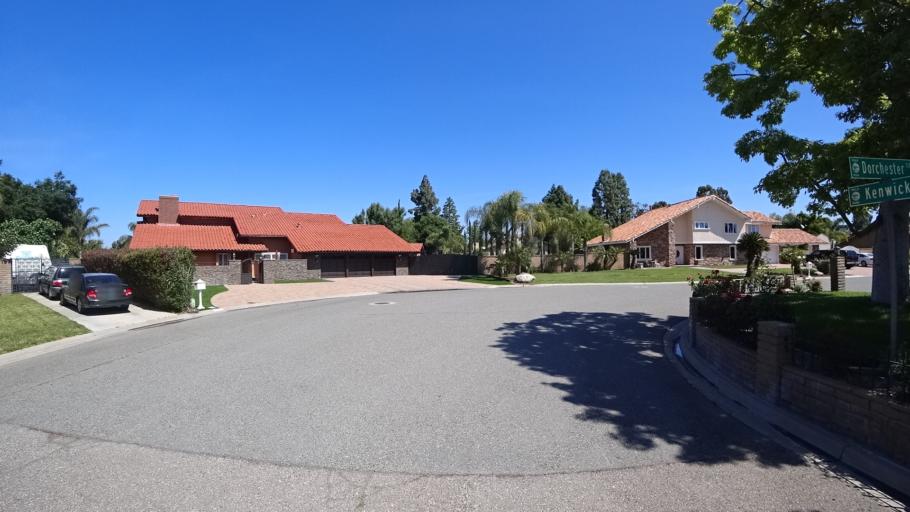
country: US
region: California
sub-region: Orange County
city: Villa Park
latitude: 33.8118
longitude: -117.8171
